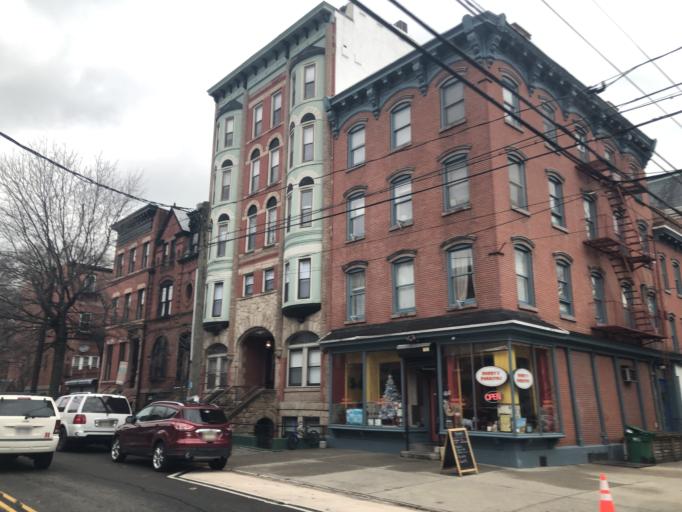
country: US
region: New Jersey
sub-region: Hudson County
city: Jersey City
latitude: 40.7173
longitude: -74.0485
